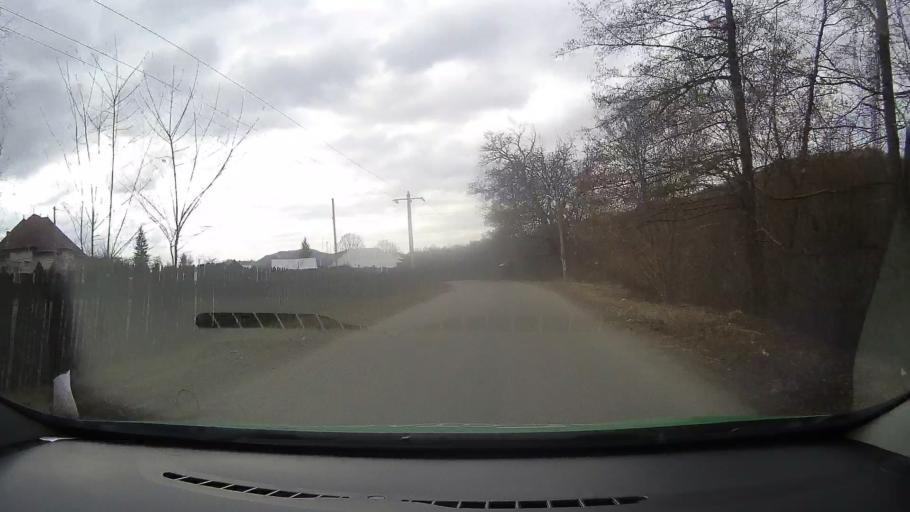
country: RO
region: Dambovita
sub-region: Comuna Valea Lunga
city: Valea Lunga-Cricov
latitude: 45.0780
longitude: 25.5756
